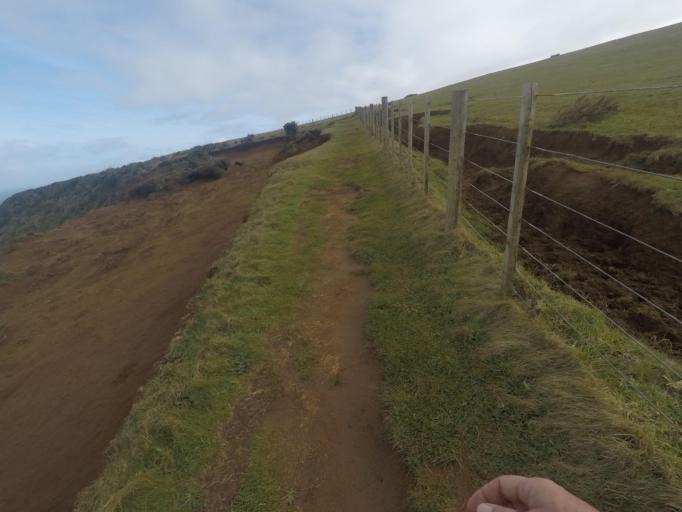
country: NZ
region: Auckland
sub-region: Auckland
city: Muriwai Beach
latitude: -36.8783
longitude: 174.4381
